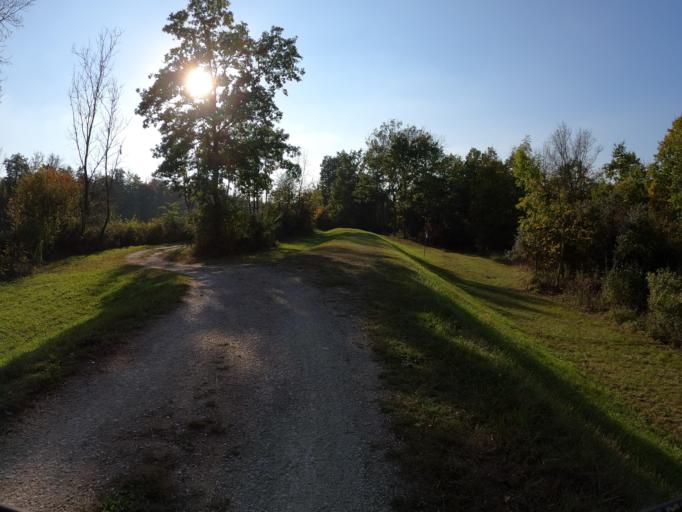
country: DE
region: Bavaria
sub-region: Swabia
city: Nersingen
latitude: 48.4442
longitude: 10.1395
